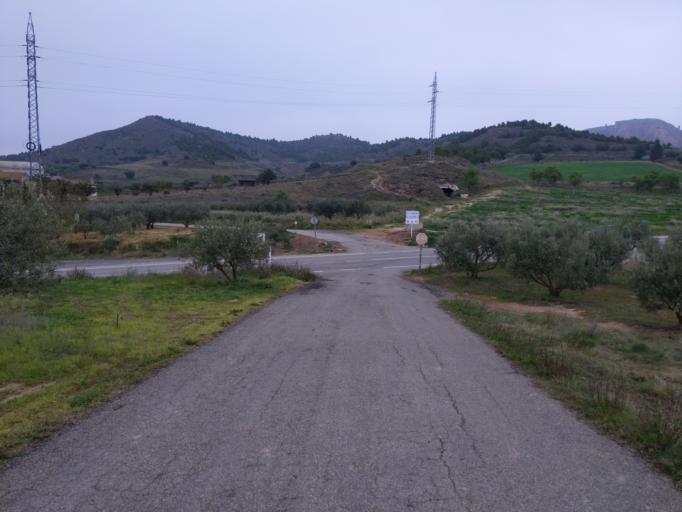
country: ES
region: La Rioja
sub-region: Provincia de La Rioja
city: Lardero
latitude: 42.4095
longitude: -2.4877
